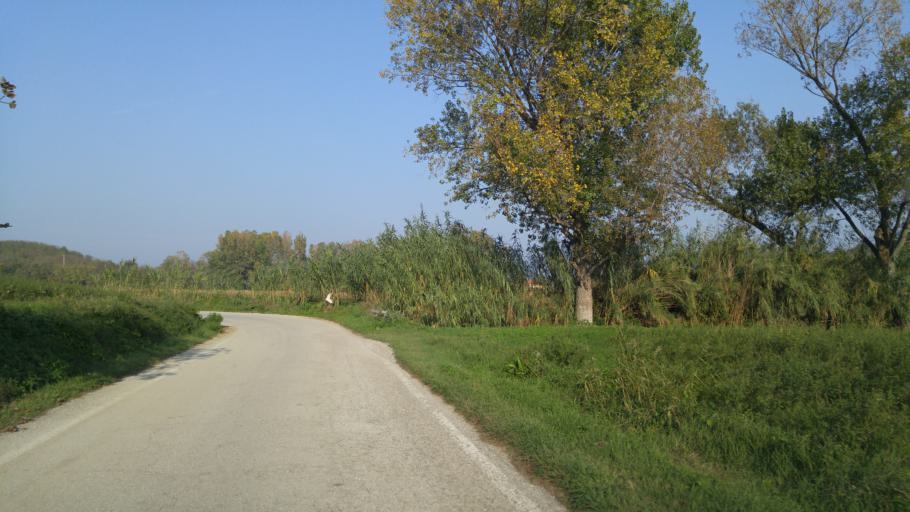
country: IT
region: The Marches
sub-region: Provincia di Pesaro e Urbino
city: Fenile
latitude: 43.8778
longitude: 12.9583
